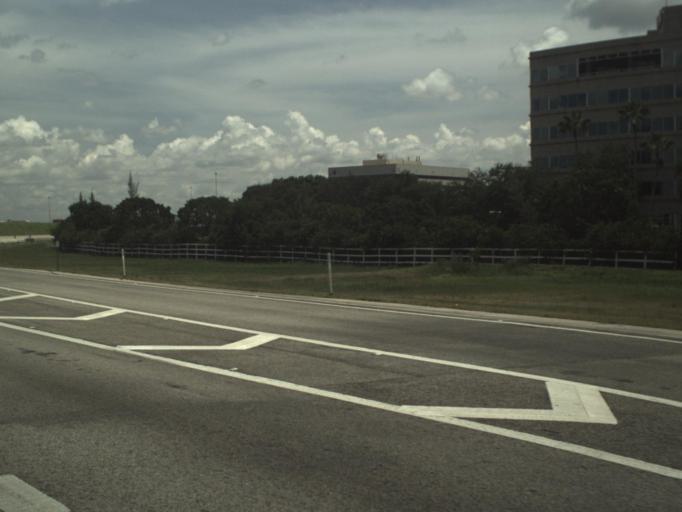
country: US
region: Florida
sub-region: Miami-Dade County
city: Palm Springs North
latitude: 25.9732
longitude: -80.3521
